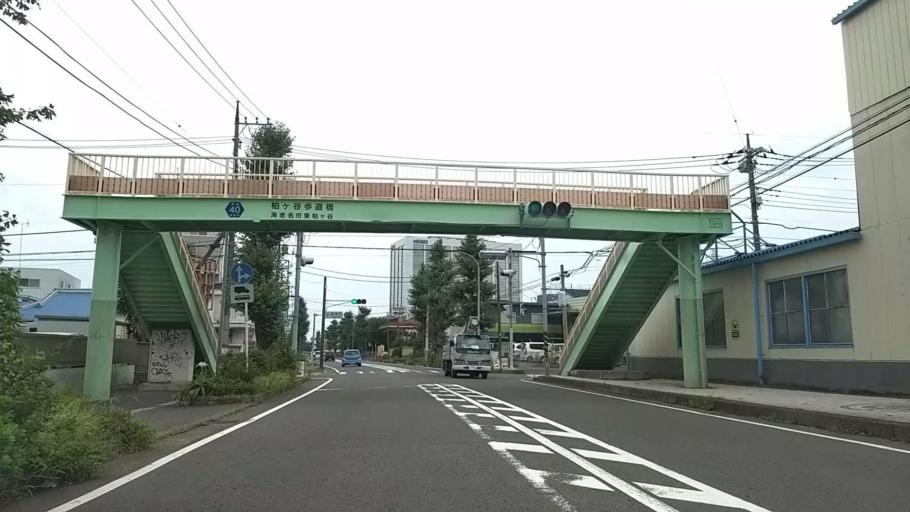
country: JP
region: Kanagawa
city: Minami-rinkan
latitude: 35.4673
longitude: 139.4299
